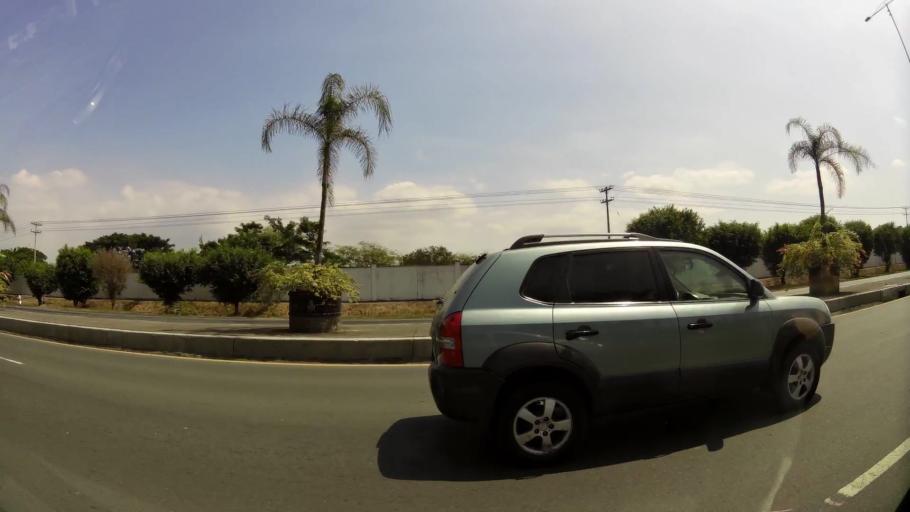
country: EC
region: Guayas
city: Eloy Alfaro
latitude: -2.0869
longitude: -79.8734
